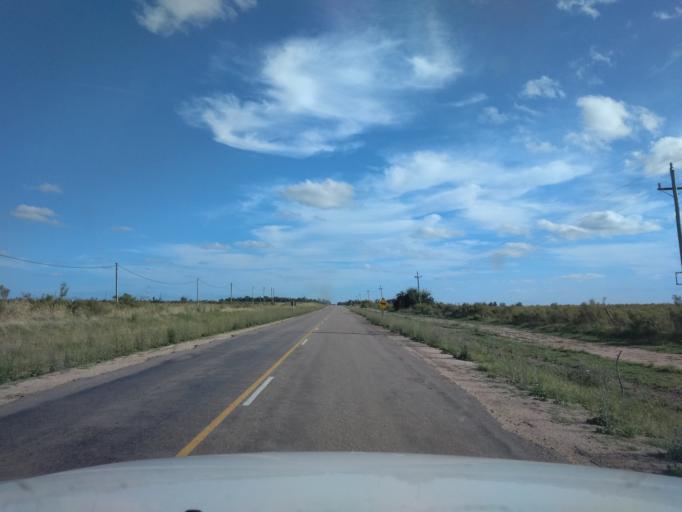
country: UY
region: Canelones
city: San Ramon
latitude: -34.2301
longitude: -55.9289
